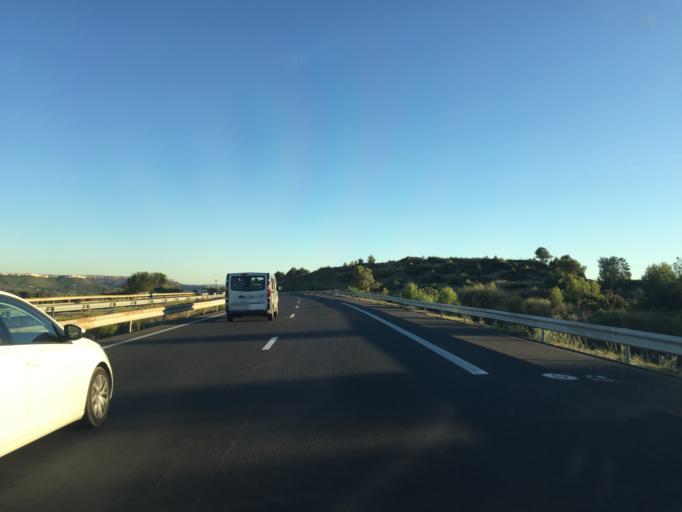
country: FR
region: Provence-Alpes-Cote d'Azur
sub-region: Departement des Bouches-du-Rhone
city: La Fare-les-Oliviers
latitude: 43.5320
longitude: 5.2185
